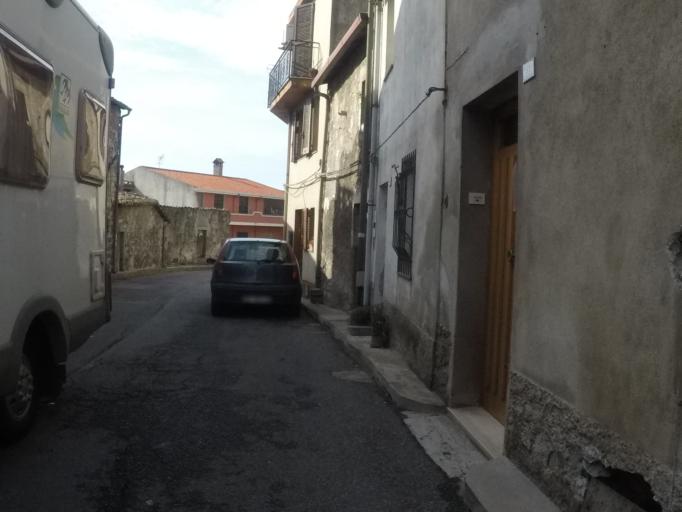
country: IT
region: Sardinia
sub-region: Provincia di Oristano
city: Santu Lussurgiu
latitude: 40.1411
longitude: 8.6512
